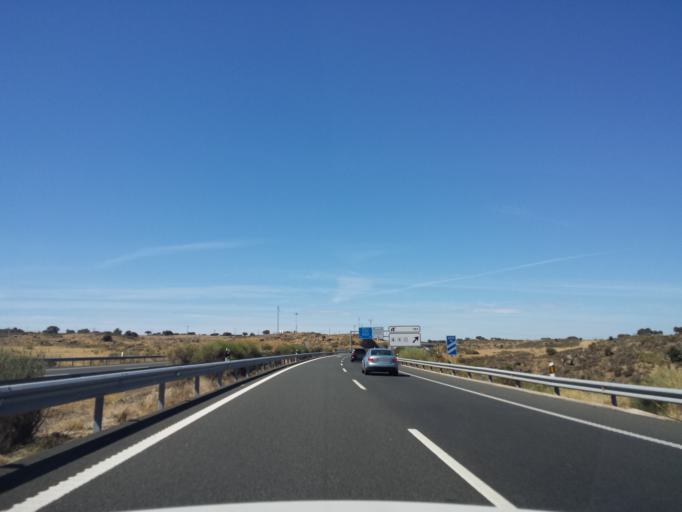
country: ES
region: Extremadura
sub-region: Provincia de Caceres
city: Navalmoral de la Mata
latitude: 39.8779
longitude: -5.5417
